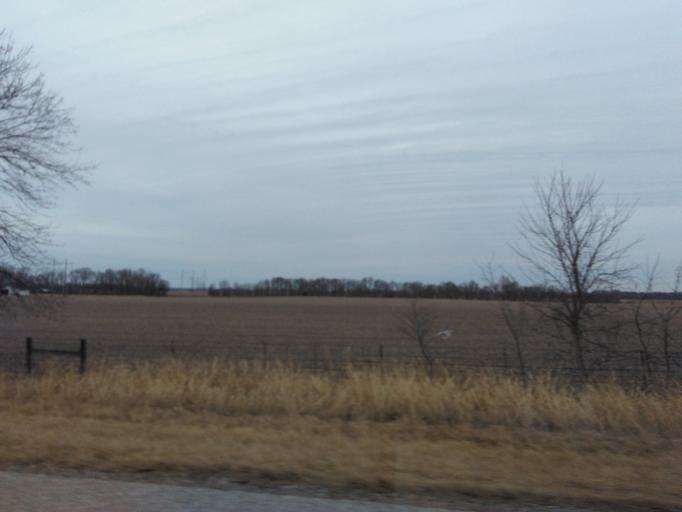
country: US
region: Illinois
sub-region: Saint Clair County
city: Lebanon
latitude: 38.5506
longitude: -89.7815
